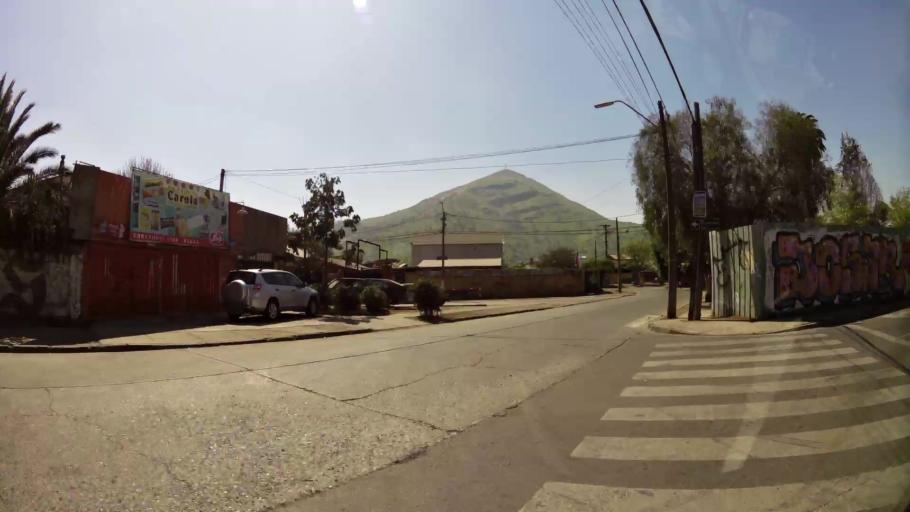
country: CL
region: Santiago Metropolitan
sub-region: Provincia de Santiago
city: Lo Prado
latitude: -33.4052
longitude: -70.7142
